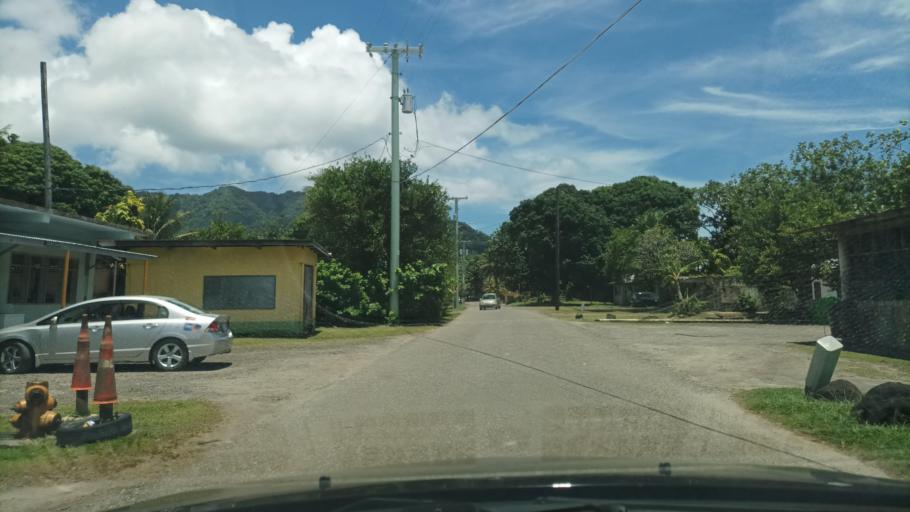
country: FM
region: Kosrae
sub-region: Lelu Municipality
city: Lelu
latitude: 5.3306
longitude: 163.0245
